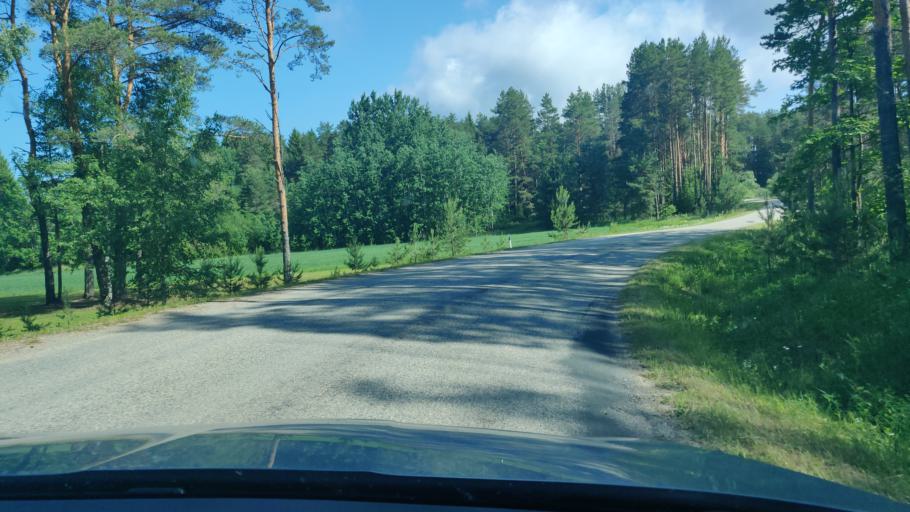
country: EE
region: Vorumaa
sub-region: Voru linn
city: Voru
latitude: 57.7346
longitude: 27.2662
